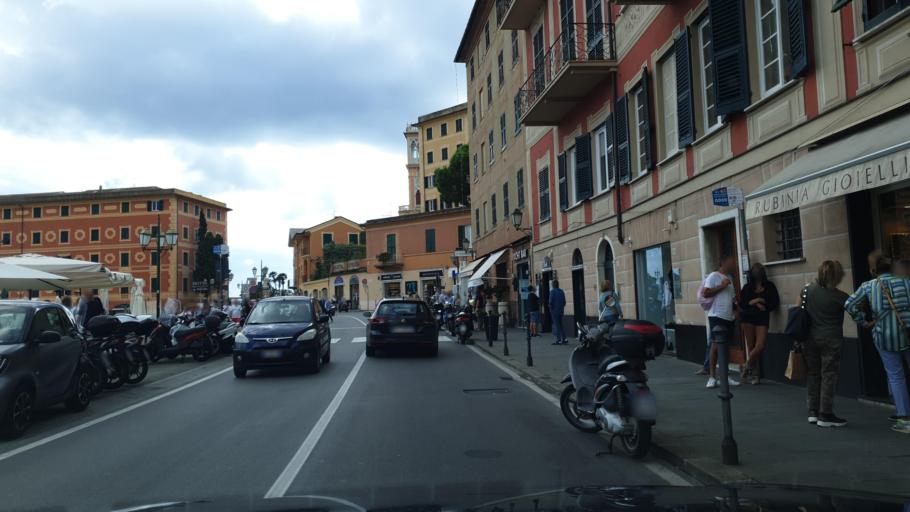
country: IT
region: Liguria
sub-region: Provincia di Genova
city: Santa Margherita Ligure
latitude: 44.3295
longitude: 9.2135
